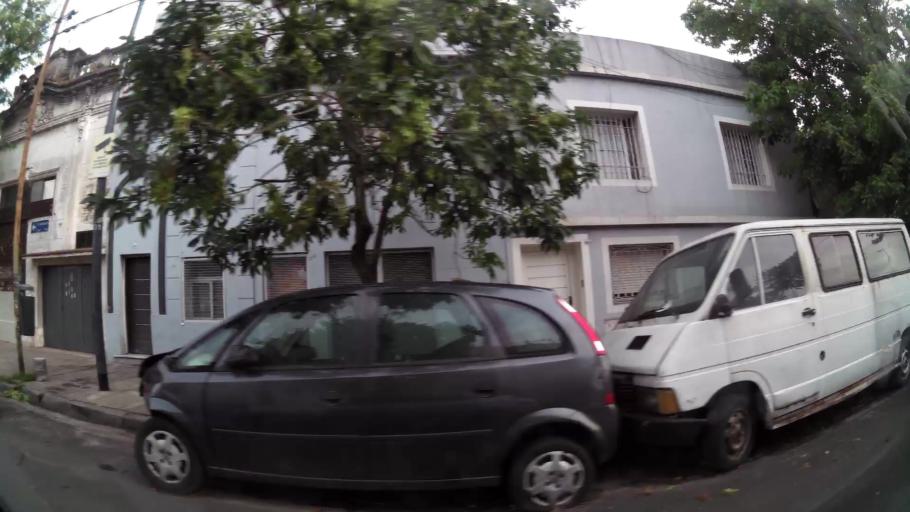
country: AR
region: Buenos Aires F.D.
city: Buenos Aires
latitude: -34.6285
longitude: -58.4200
